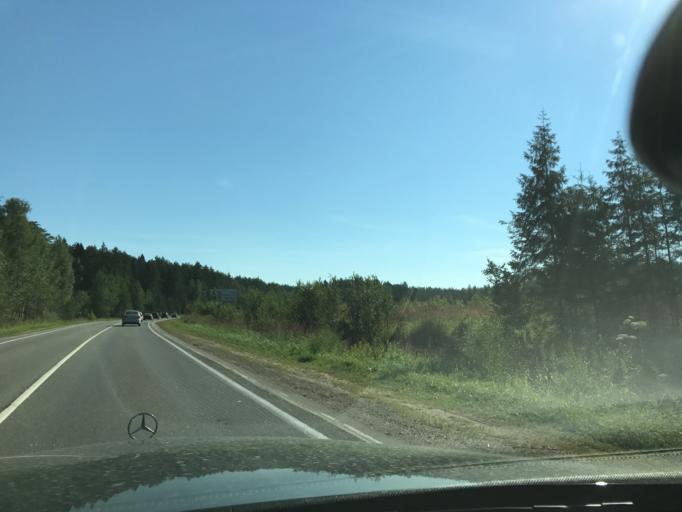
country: RU
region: Vladimir
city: Kirzhach
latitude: 56.1092
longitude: 38.6959
